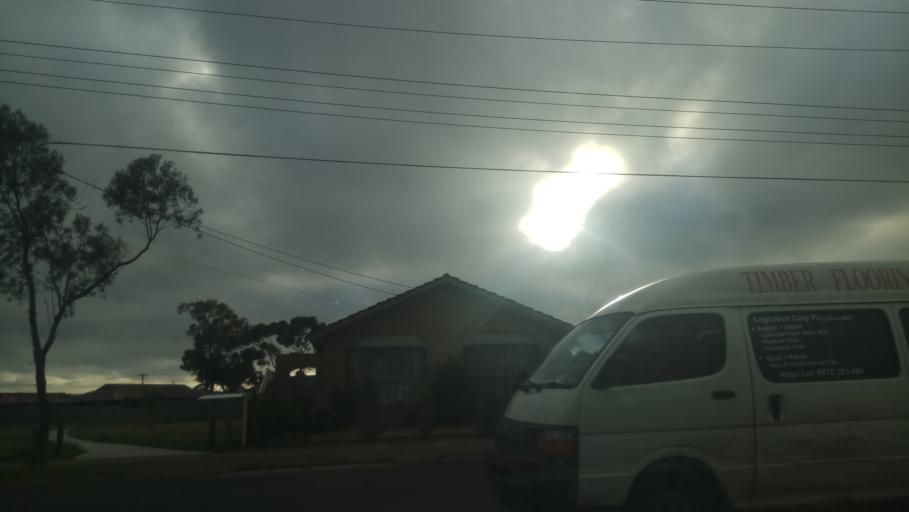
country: AU
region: Victoria
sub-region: Hobsons Bay
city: Altona Meadows
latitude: -37.8844
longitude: 144.7853
